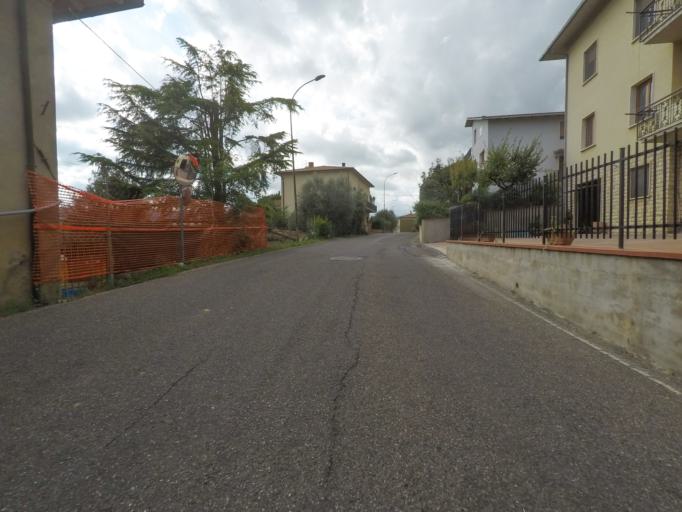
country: IT
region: Tuscany
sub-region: Provincia di Siena
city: Torrita di Siena
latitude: 43.1638
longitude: 11.7717
